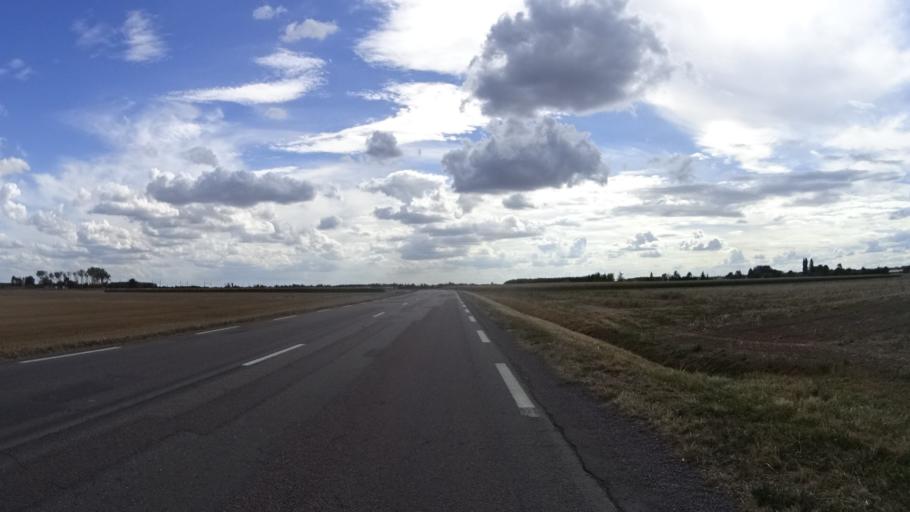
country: FR
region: Bourgogne
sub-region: Departement de la Cote-d'Or
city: Seurre
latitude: 47.0226
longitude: 5.1671
